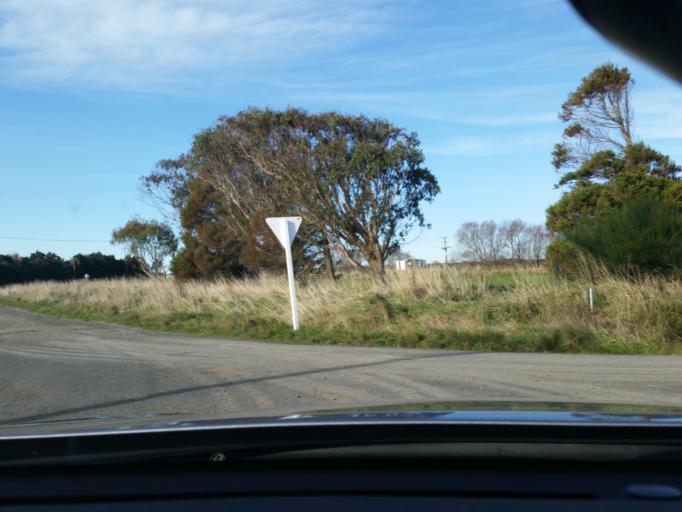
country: NZ
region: Southland
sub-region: Southland District
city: Riverton
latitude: -46.3109
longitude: 168.0153
